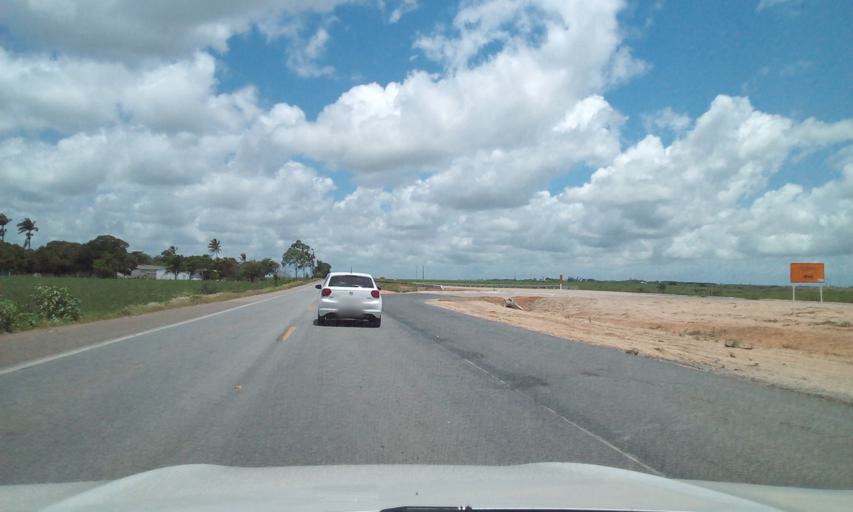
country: BR
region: Alagoas
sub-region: Sao Miguel Dos Campos
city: Sao Miguel dos Campos
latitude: -9.9008
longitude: -36.2112
